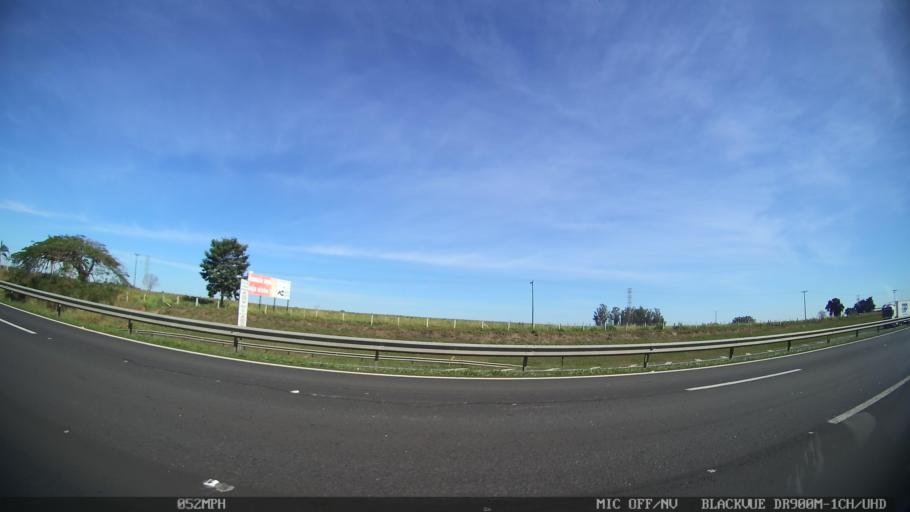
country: BR
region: Sao Paulo
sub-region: Pirassununga
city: Pirassununga
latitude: -22.0836
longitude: -47.4207
